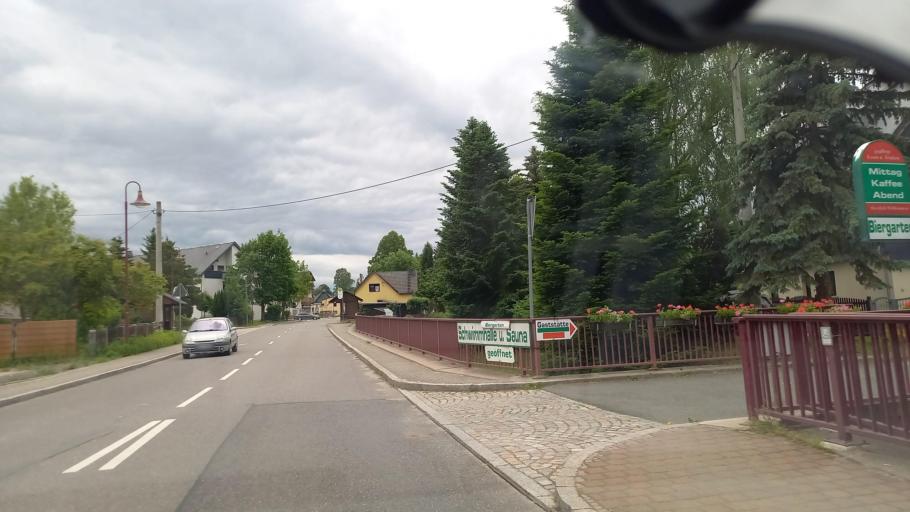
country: DE
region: Saxony
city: Kirchberg
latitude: 50.5939
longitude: 12.5466
